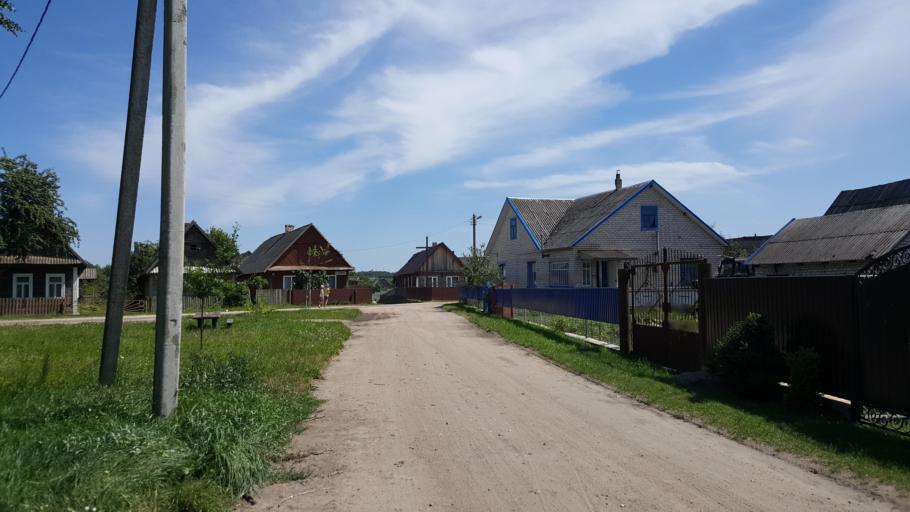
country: BY
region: Brest
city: Pruzhany
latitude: 52.5523
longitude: 24.2182
